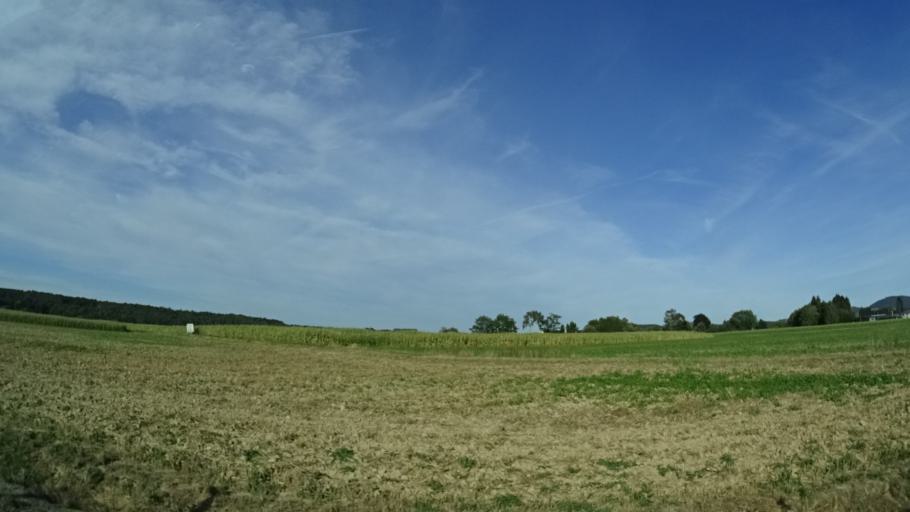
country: DE
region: Hesse
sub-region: Regierungsbezirk Kassel
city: Dipperz
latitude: 50.5422
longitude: 9.7838
